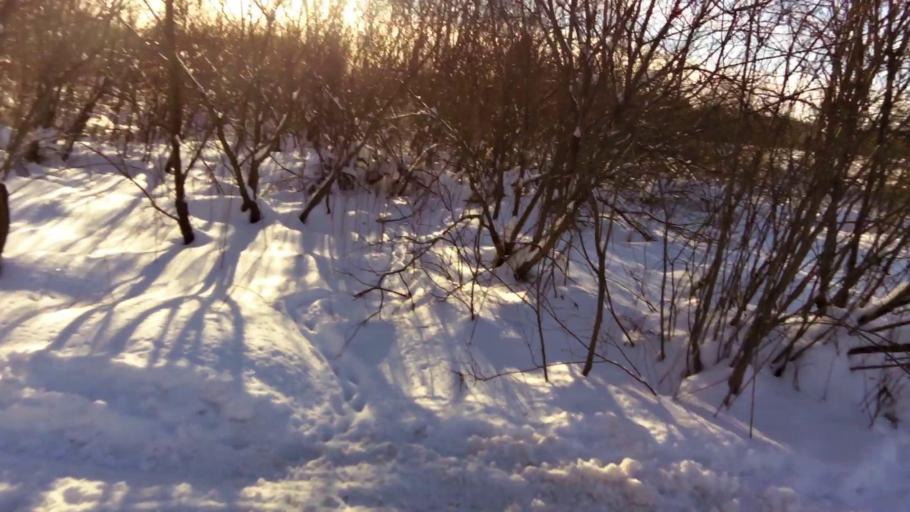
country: US
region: New York
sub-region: Chautauqua County
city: Mayville
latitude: 42.2431
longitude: -79.3956
